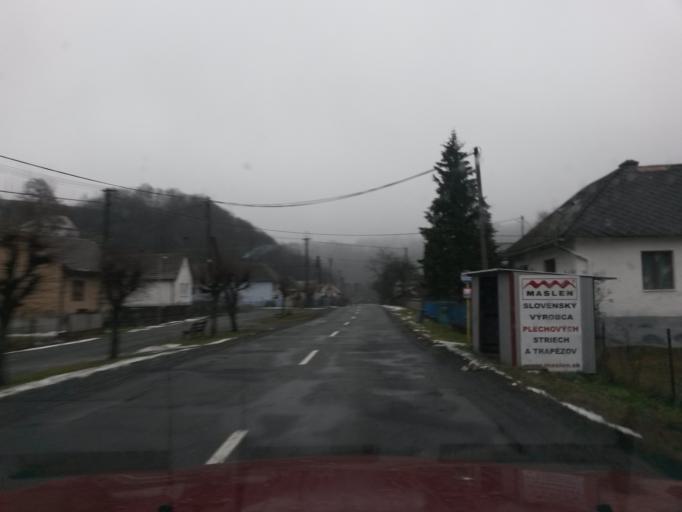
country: SK
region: Presovsky
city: Vranov nad Topl'ou
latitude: 49.0133
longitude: 21.7586
